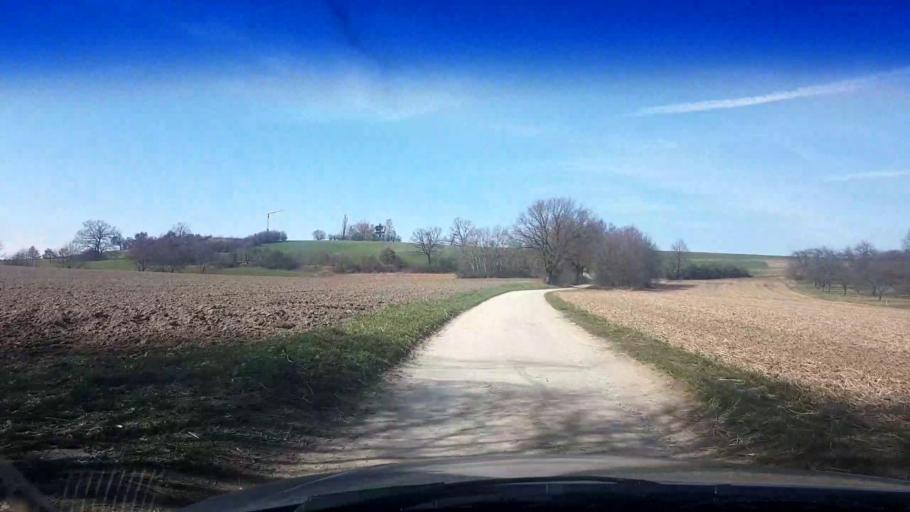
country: DE
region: Bavaria
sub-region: Upper Franconia
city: Bischberg
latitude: 49.8969
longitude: 10.8270
